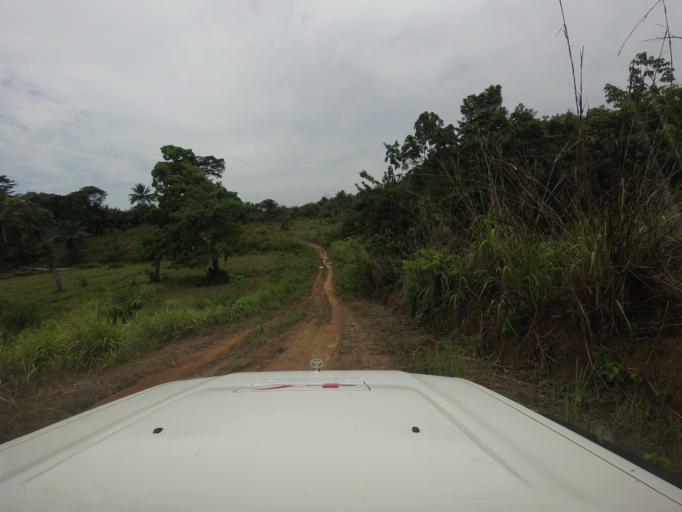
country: SL
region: Eastern Province
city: Buedu
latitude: 8.2529
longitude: -10.2883
